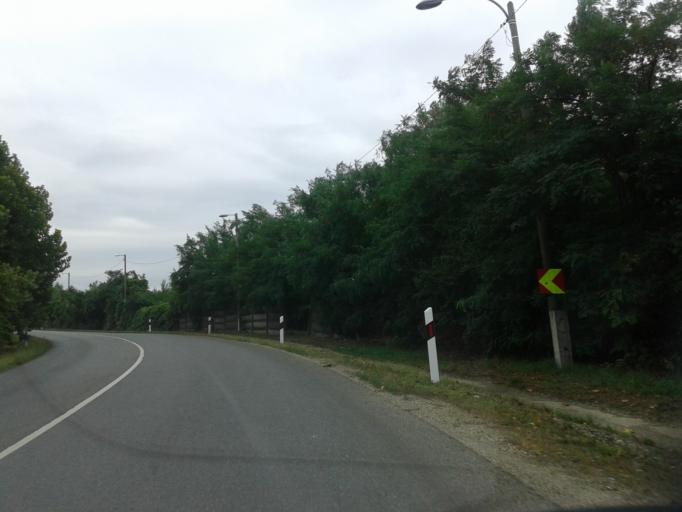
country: HU
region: Pest
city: Halasztelek
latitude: 47.3519
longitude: 18.9812
